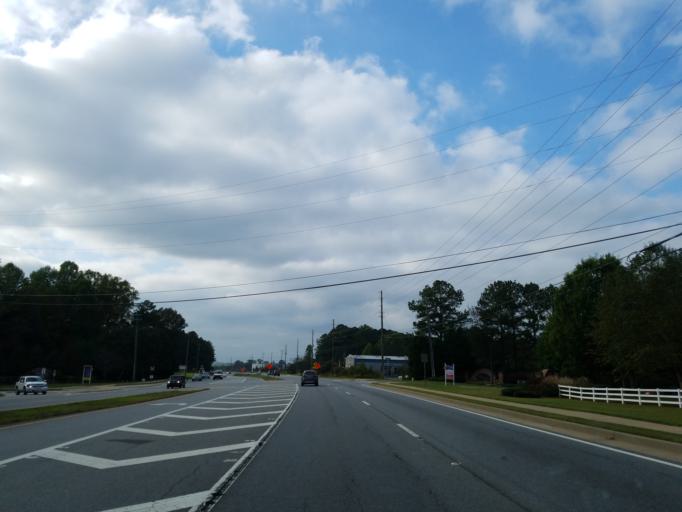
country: US
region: Georgia
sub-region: Cobb County
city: Acworth
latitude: 34.0956
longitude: -84.6235
